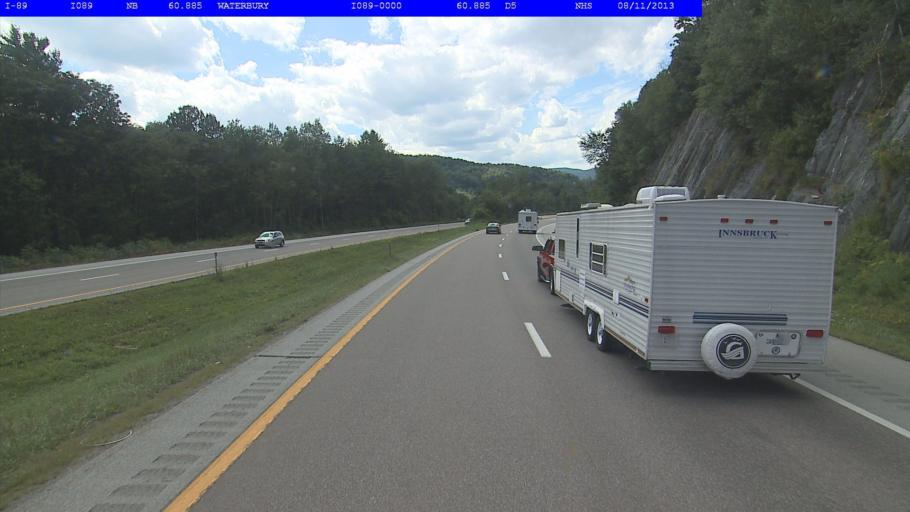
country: US
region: Vermont
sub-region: Washington County
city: Waterbury
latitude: 44.3146
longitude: -72.7152
